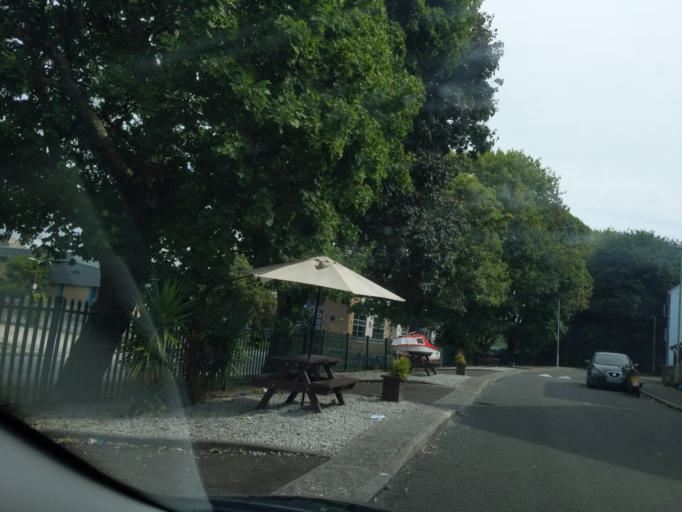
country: GB
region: England
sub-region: Plymouth
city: Plymstock
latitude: 50.3808
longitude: -4.1126
